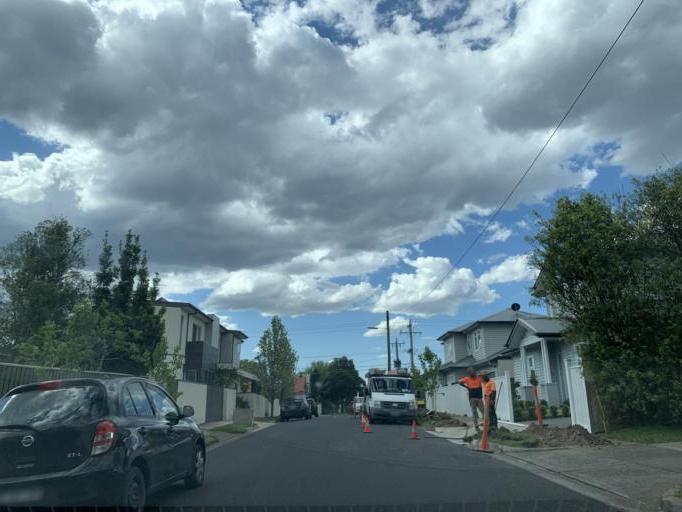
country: AU
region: Victoria
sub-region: Bayside
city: Hampton
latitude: -37.9405
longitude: 145.0147
